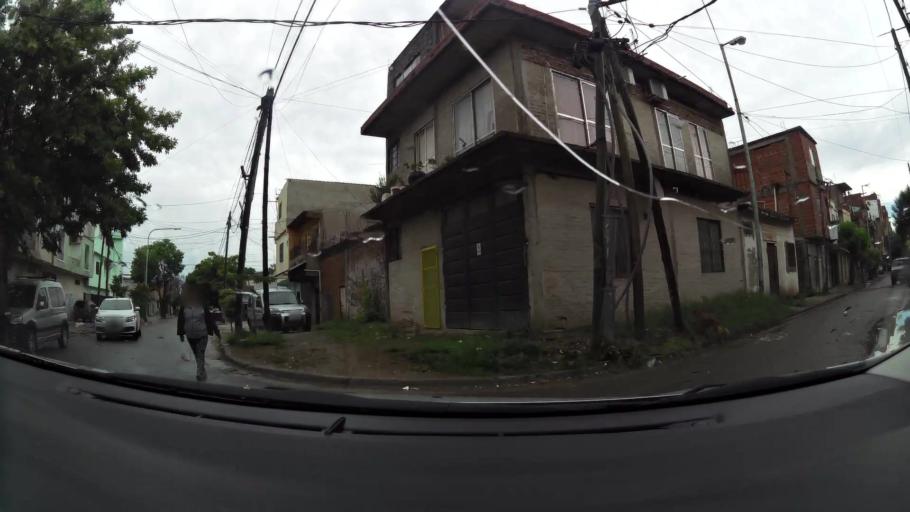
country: AR
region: Buenos Aires F.D.
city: Villa Lugano
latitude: -34.6611
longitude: -58.4526
